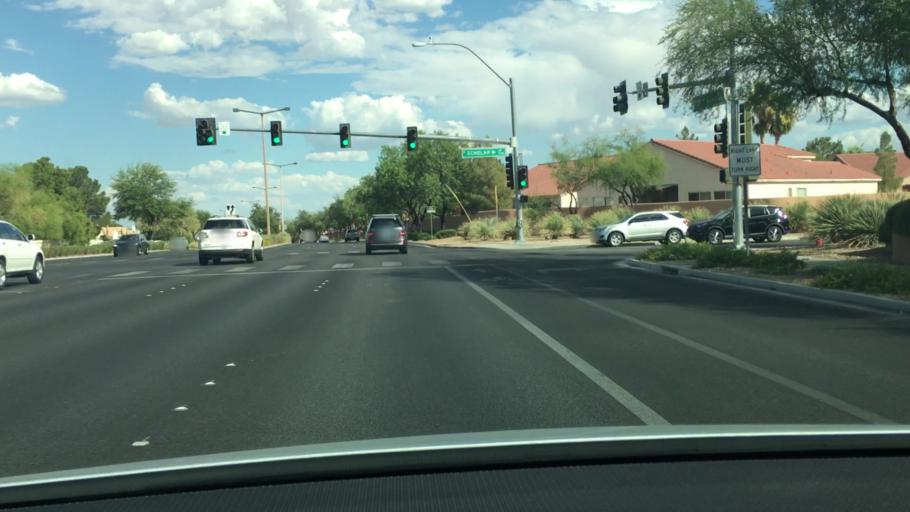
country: US
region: Nevada
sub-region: Clark County
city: Summerlin South
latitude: 36.1978
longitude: -115.2791
